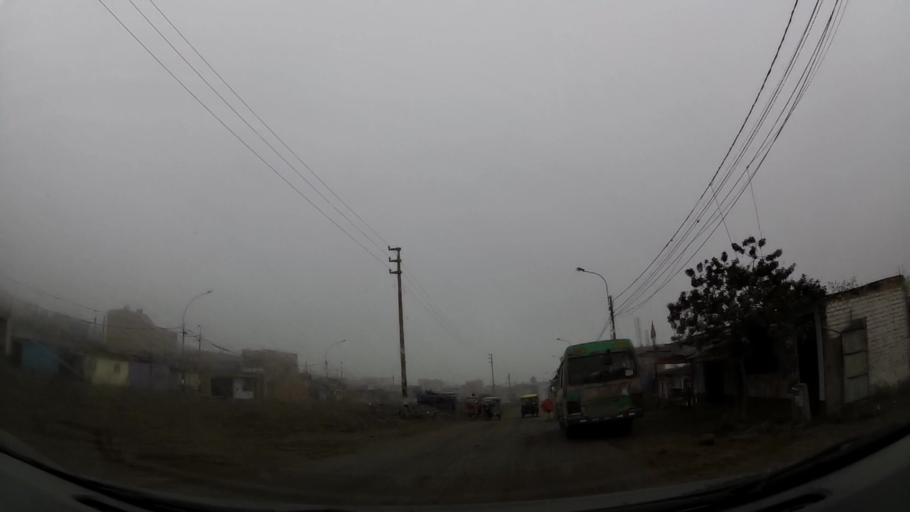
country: PE
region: Lima
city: Ventanilla
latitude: -11.8361
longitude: -77.1385
